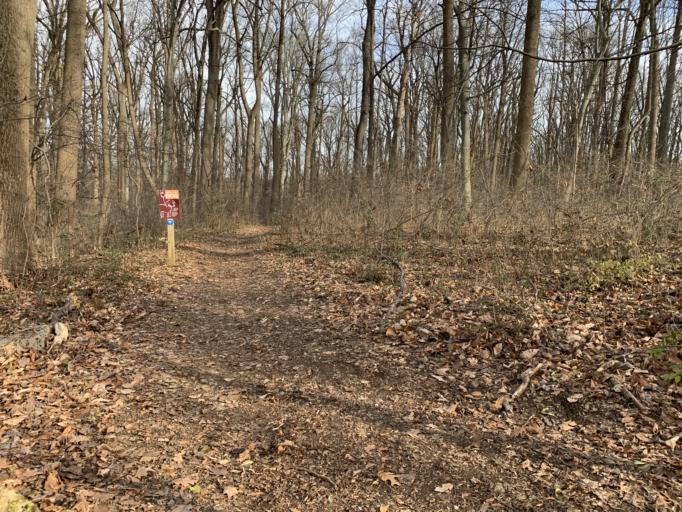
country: US
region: Pennsylvania
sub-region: Chester County
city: Malvern
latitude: 40.0046
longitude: -75.5249
